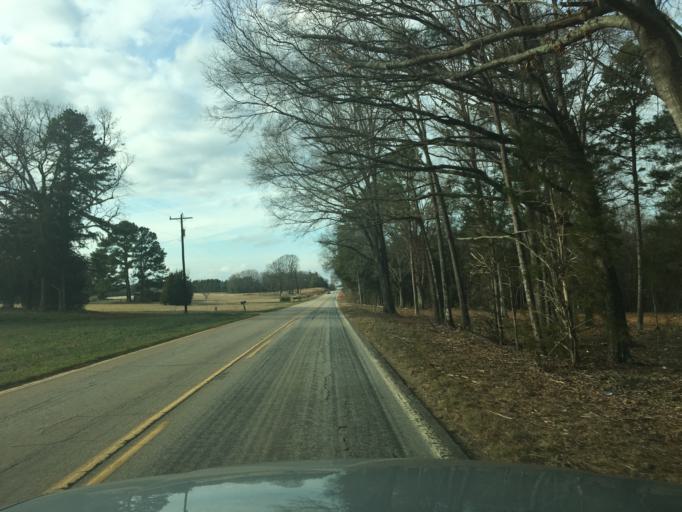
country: US
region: South Carolina
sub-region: Abbeville County
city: Due West
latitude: 34.3378
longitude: -82.4881
